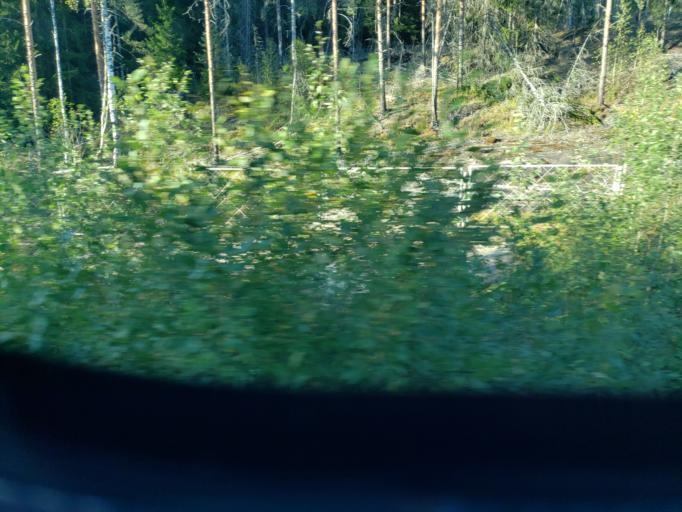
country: FI
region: South Karelia
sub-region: Lappeenranta
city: Nuijamaa
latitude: 60.8542
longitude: 28.3450
